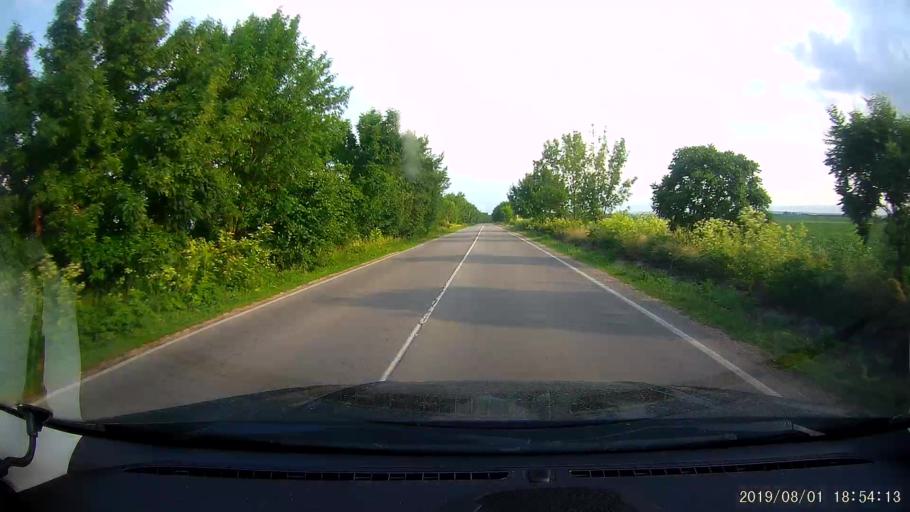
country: BG
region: Shumen
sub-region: Obshtina Shumen
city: Shumen
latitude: 43.2040
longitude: 27.0004
